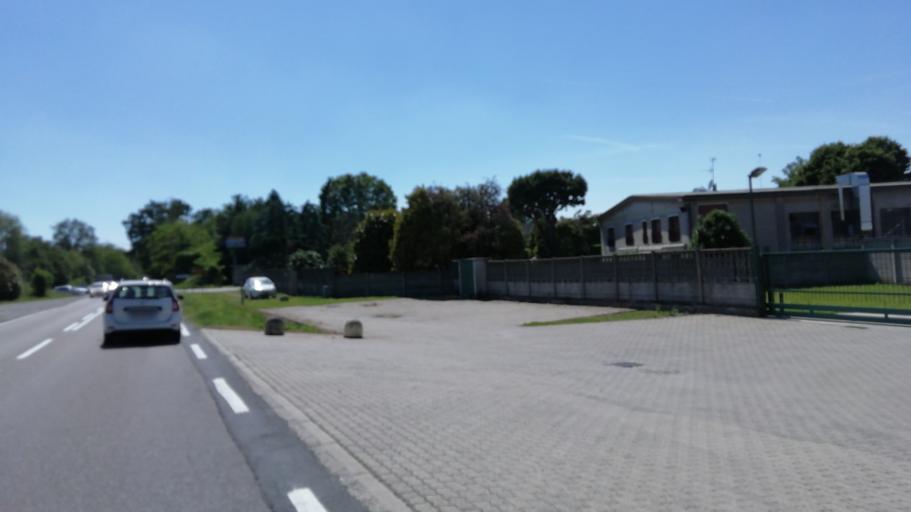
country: IT
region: Lombardy
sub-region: Provincia di Varese
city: Lonate Pozzolo
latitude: 45.5914
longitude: 8.7366
